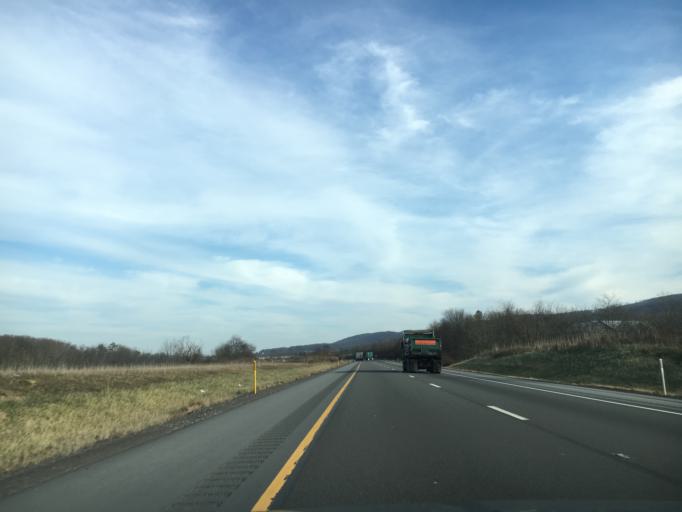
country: US
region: Pennsylvania
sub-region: Montour County
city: Mechanicsville
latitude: 41.0013
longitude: -76.5838
